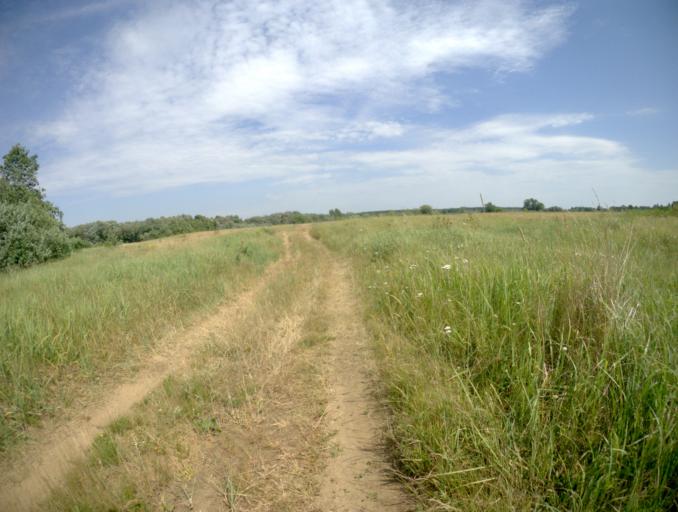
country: RU
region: Vladimir
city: Vorsha
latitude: 56.0337
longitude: 40.1843
